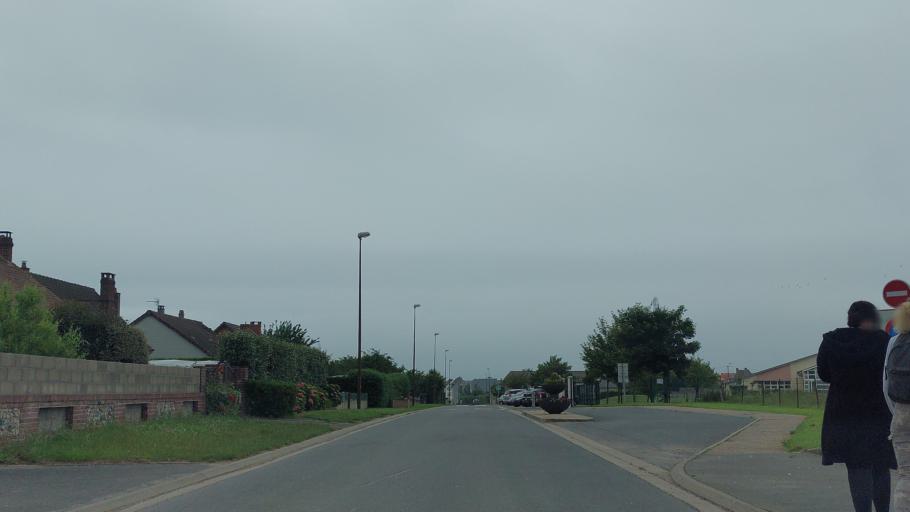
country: FR
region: Picardie
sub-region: Departement de la Somme
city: Ault
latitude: 50.1000
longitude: 1.4576
